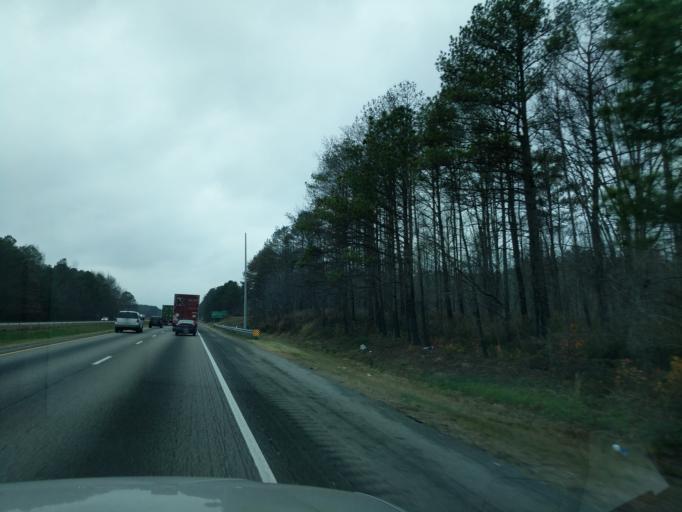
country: US
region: Georgia
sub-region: Gwinnett County
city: Dacula
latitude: 34.0765
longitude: -83.9016
